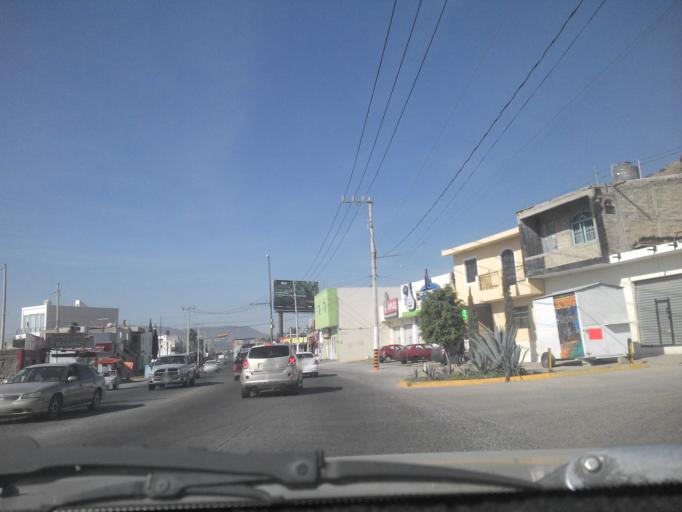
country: MX
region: Jalisco
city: Guadalajara
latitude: 20.6567
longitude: -103.4523
